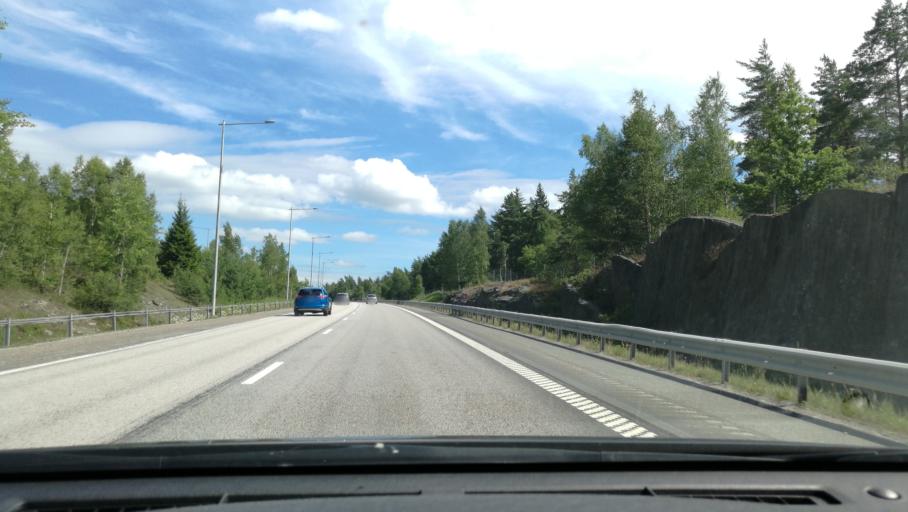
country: SE
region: Stockholm
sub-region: Upplands-Bro Kommun
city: Bro
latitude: 59.5116
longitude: 17.6870
